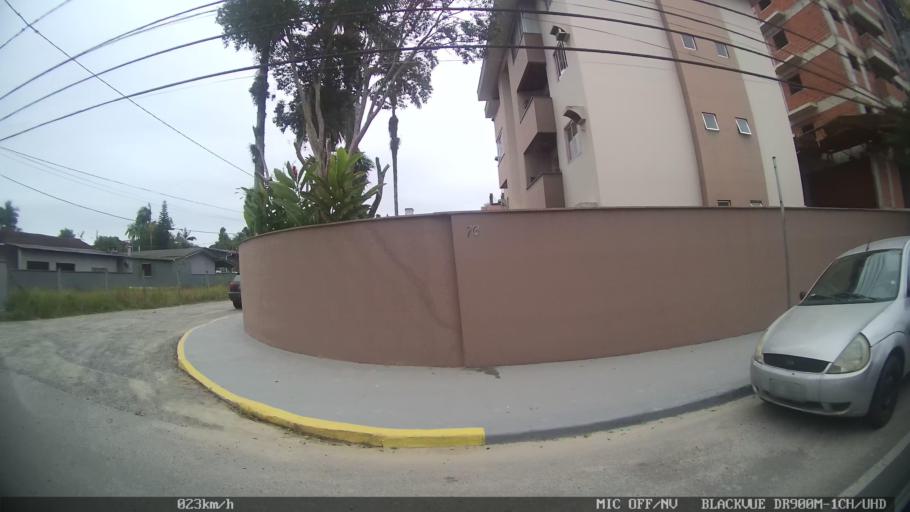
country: BR
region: Santa Catarina
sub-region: Joinville
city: Joinville
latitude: -26.2676
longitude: -48.8441
